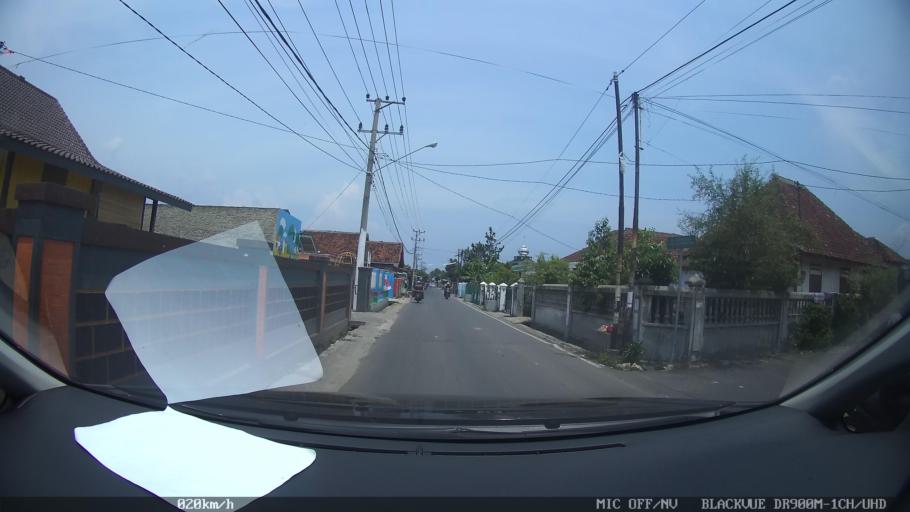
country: ID
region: Lampung
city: Bandarlampung
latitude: -5.4469
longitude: 105.2538
